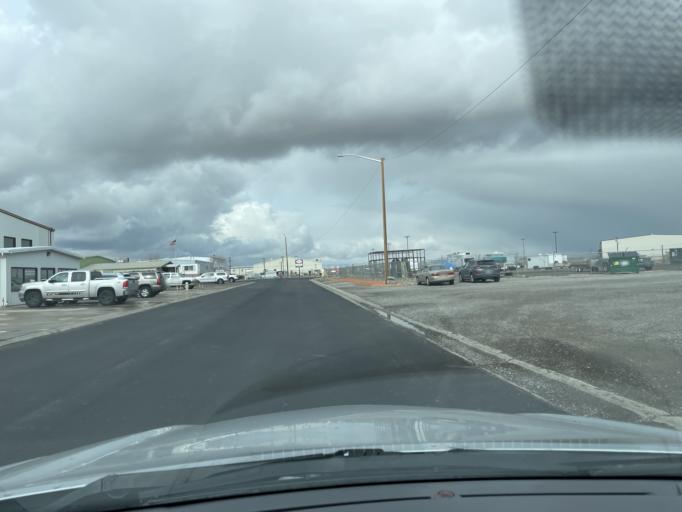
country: US
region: Colorado
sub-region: Mesa County
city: Redlands
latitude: 39.1083
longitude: -108.6322
